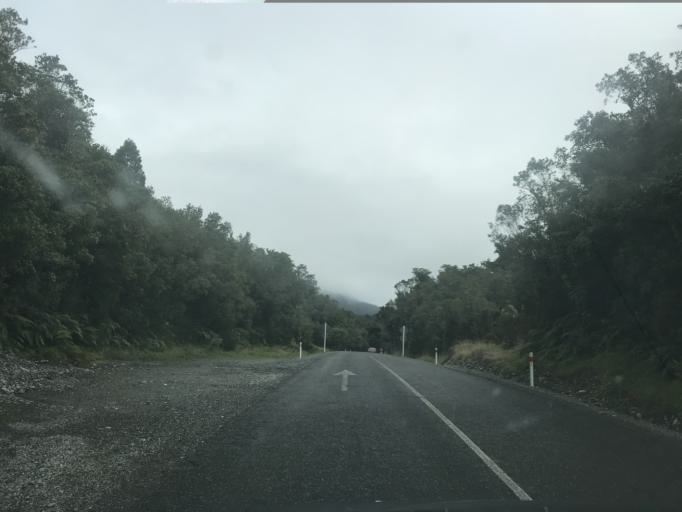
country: NZ
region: West Coast
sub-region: Westland District
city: Hokitika
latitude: -42.9533
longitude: 171.0229
